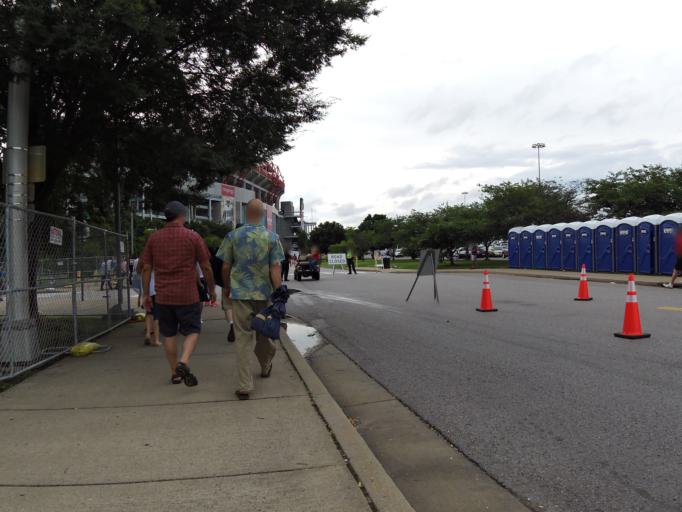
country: US
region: Tennessee
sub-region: Davidson County
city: Nashville
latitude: 36.1653
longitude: -86.7685
